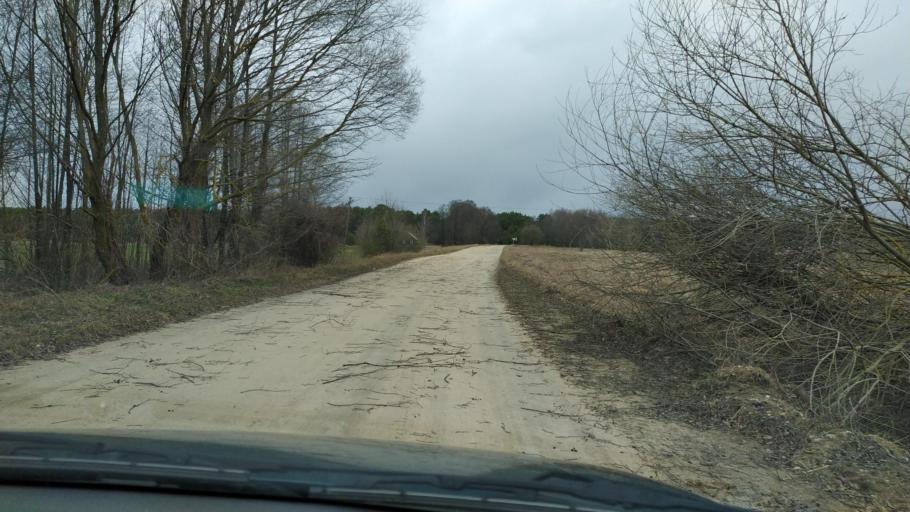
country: BY
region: Brest
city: Kamyanyets
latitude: 52.4082
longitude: 24.0101
